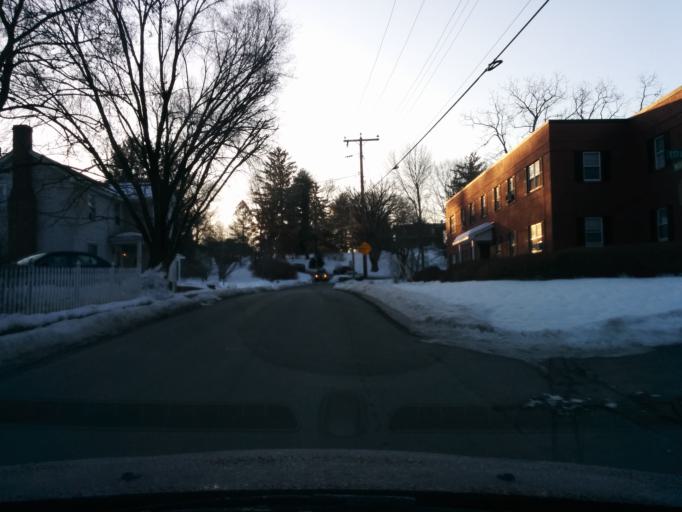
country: US
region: Virginia
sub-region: City of Lexington
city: Lexington
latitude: 37.7829
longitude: -79.4386
